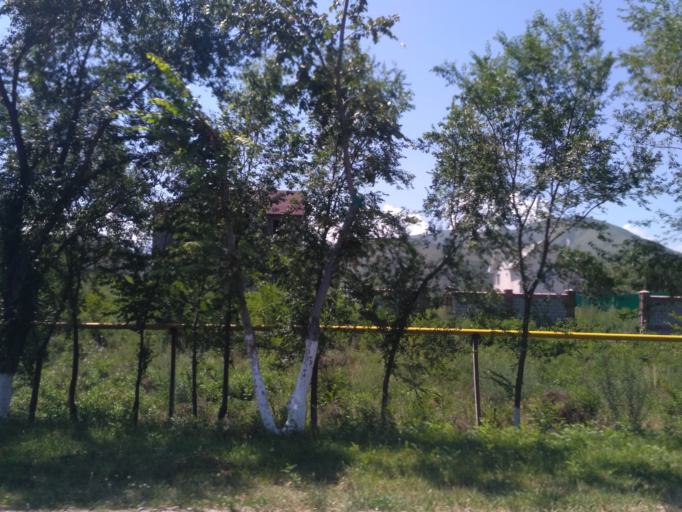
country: KZ
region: Almaty Oblysy
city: Burunday
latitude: 43.1662
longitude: 76.6007
